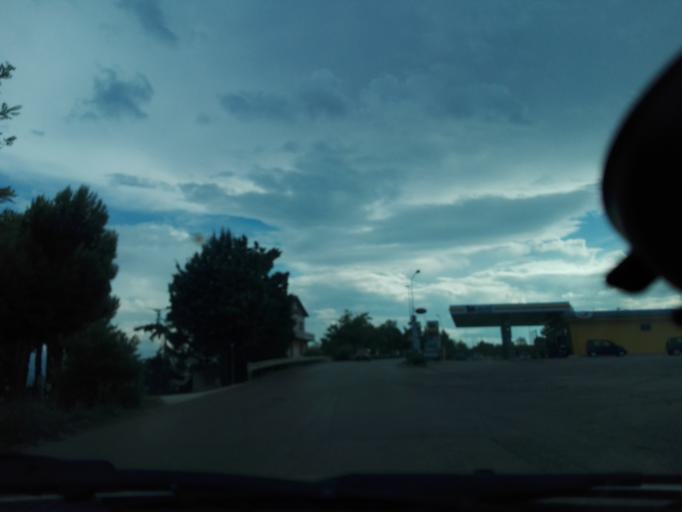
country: IT
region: Abruzzo
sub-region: Provincia di Pescara
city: Cappelle sul Tavo
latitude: 42.4594
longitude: 14.1170
